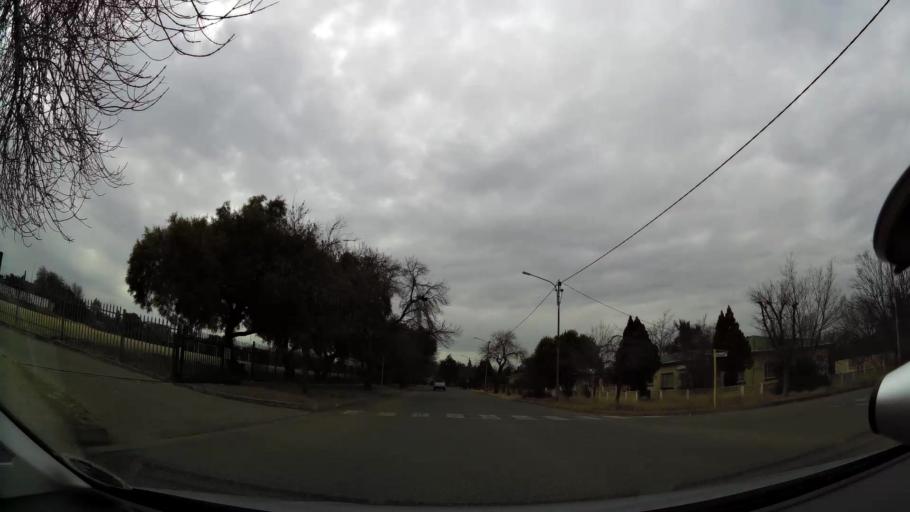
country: ZA
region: Orange Free State
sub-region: Fezile Dabi District Municipality
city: Kroonstad
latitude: -27.6437
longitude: 27.2364
